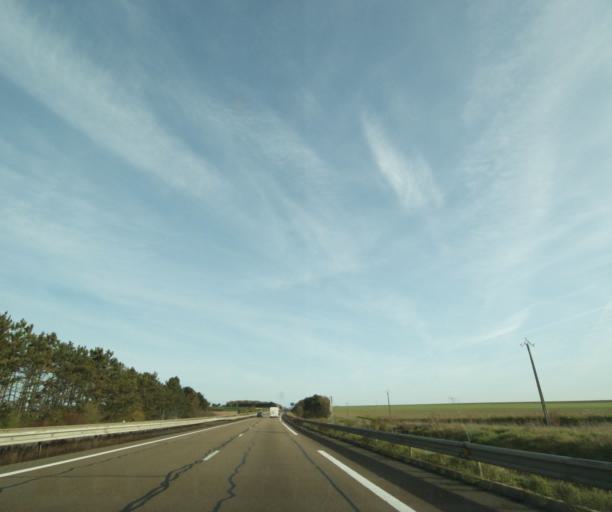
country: FR
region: Champagne-Ardenne
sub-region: Departement de la Marne
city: Fagnieres
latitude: 49.0464
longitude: 4.3090
